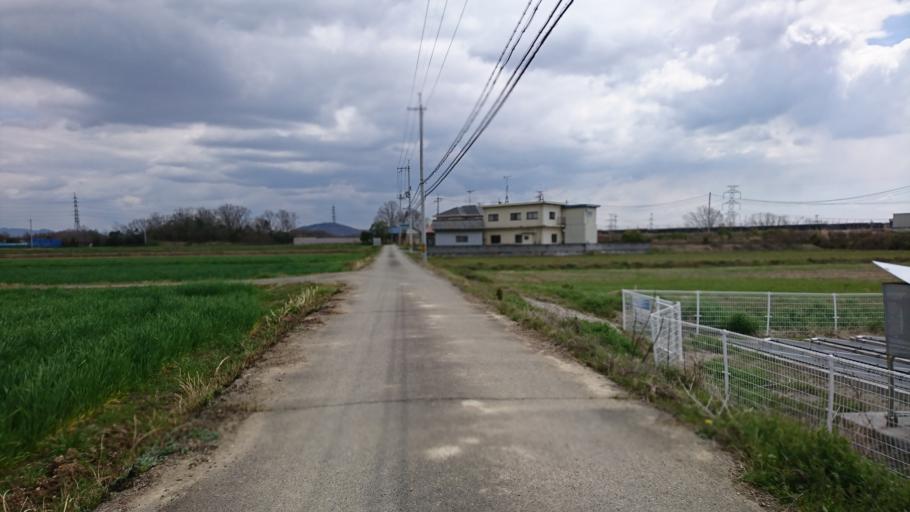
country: JP
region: Hyogo
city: Miki
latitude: 34.7701
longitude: 134.9574
